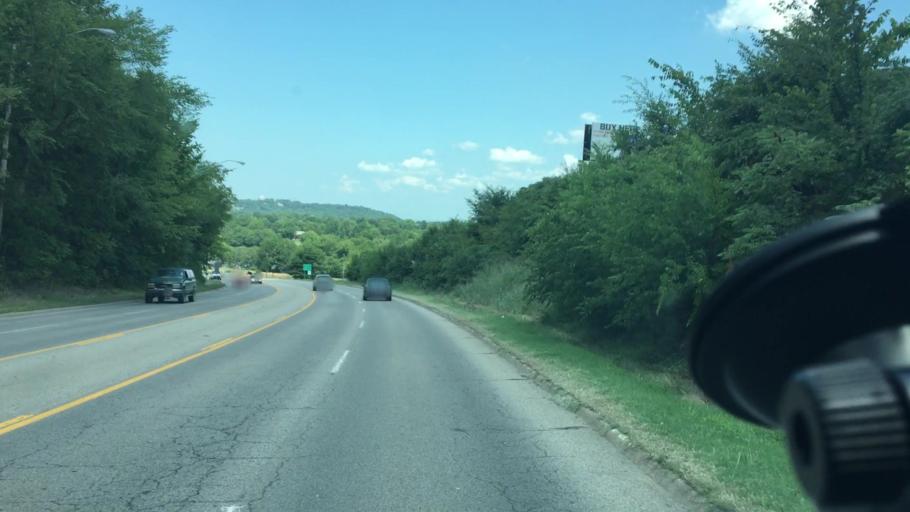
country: US
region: Arkansas
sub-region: Sebastian County
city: Barling
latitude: 35.3394
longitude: -94.3201
